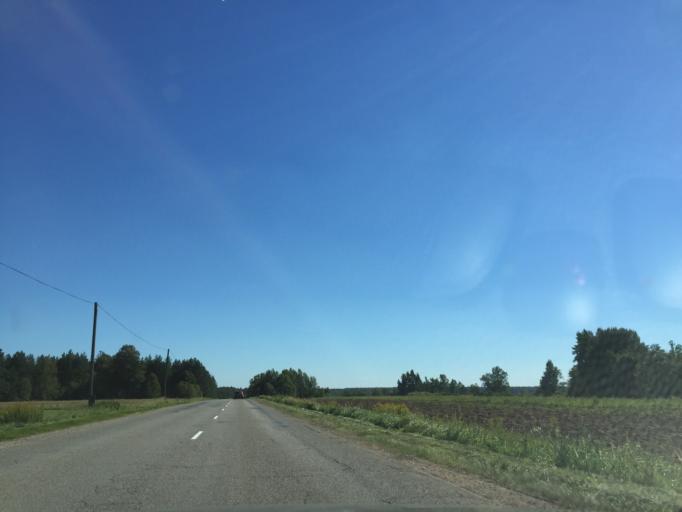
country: LV
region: Akniste
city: Akniste
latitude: 56.1328
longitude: 25.8253
